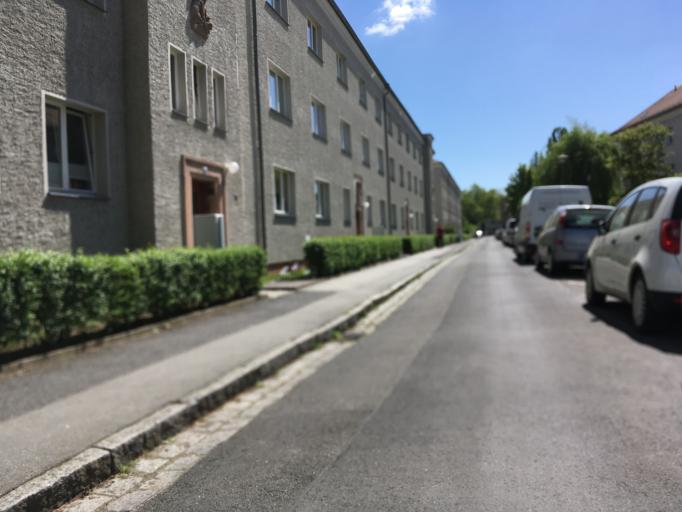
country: DE
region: Saxony
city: Radebeul
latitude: 51.0942
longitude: 13.7093
